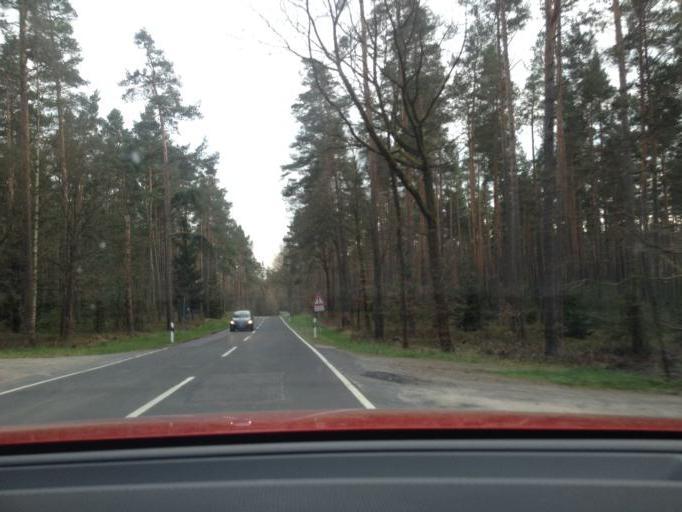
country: DE
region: Bavaria
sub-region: Upper Palatinate
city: Speinshart
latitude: 49.7997
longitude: 11.8202
